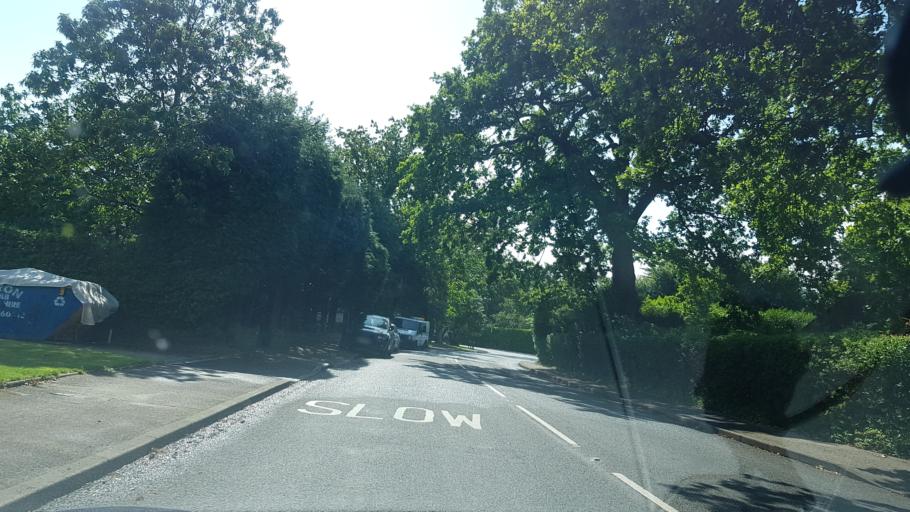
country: GB
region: England
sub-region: Surrey
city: West Byfleet
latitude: 51.3302
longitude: -0.5093
